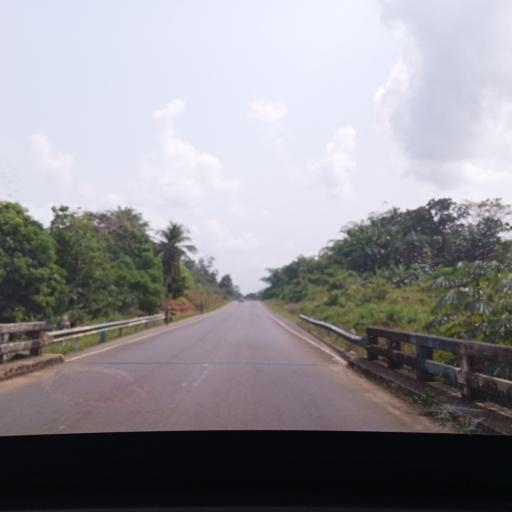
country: LR
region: Margibi
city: Kakata
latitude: 6.2523
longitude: -10.3012
